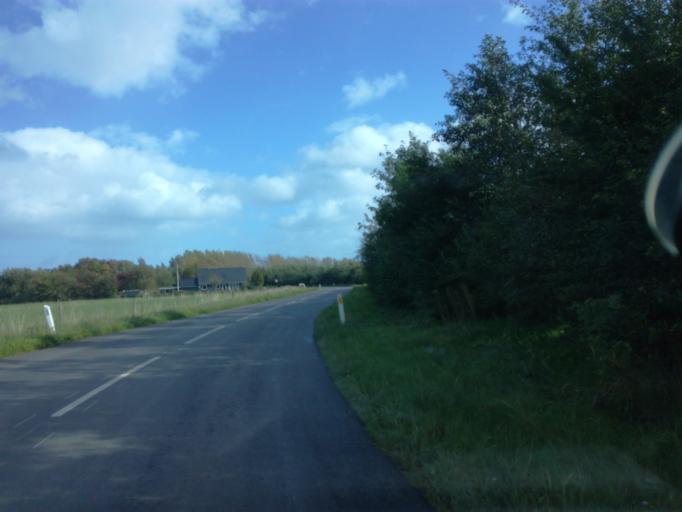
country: DK
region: South Denmark
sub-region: Fredericia Kommune
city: Fredericia
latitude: 55.5824
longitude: 9.7087
